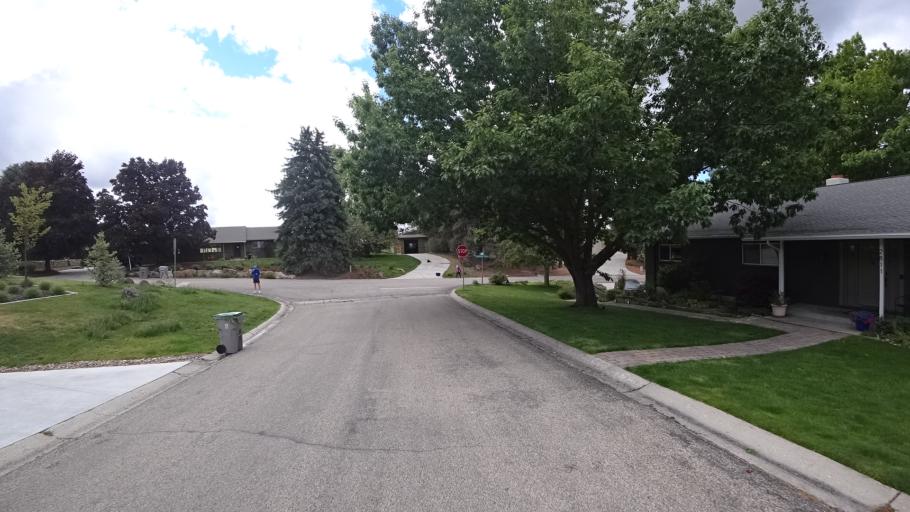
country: US
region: Idaho
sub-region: Ada County
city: Boise
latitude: 43.6455
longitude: -116.1841
